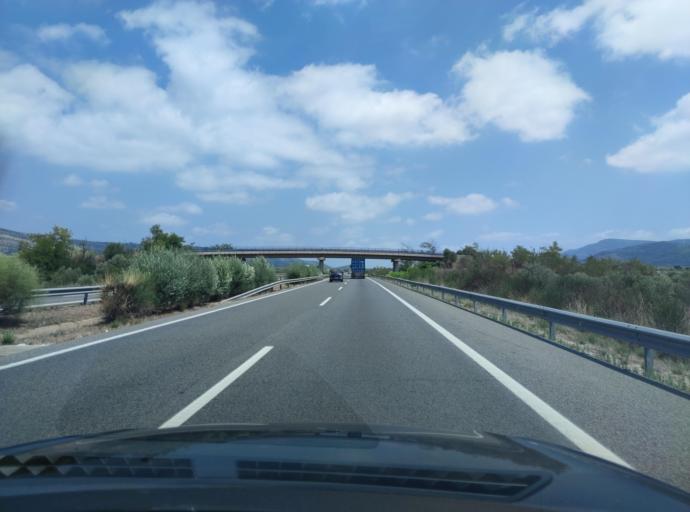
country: ES
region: Catalonia
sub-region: Provincia de Tarragona
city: Ulldecona
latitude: 40.5988
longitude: 0.4713
